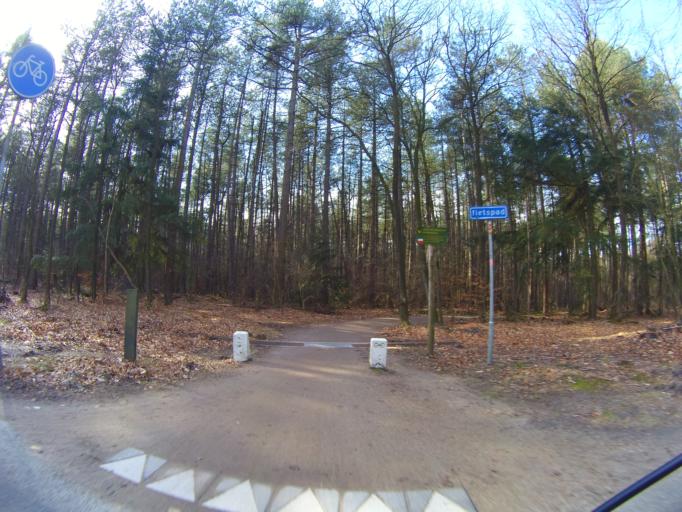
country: NL
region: North Holland
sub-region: Gemeente Bussum
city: Bussum
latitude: 52.2536
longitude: 5.1617
